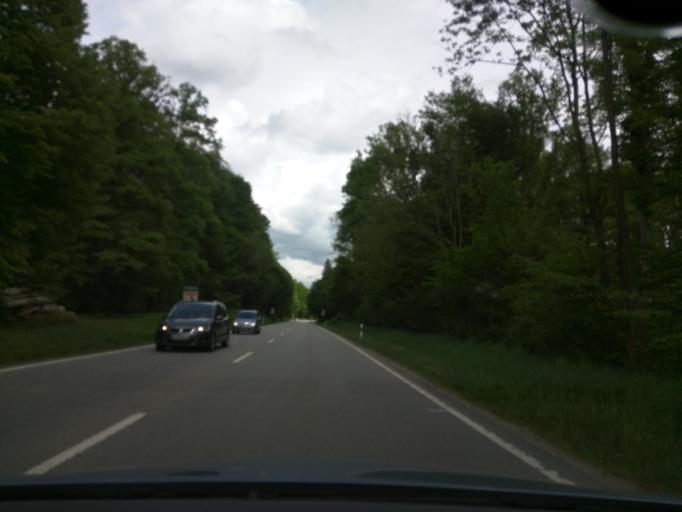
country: DE
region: Bavaria
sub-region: Lower Bavaria
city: Passau
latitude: 48.5452
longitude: 13.4065
